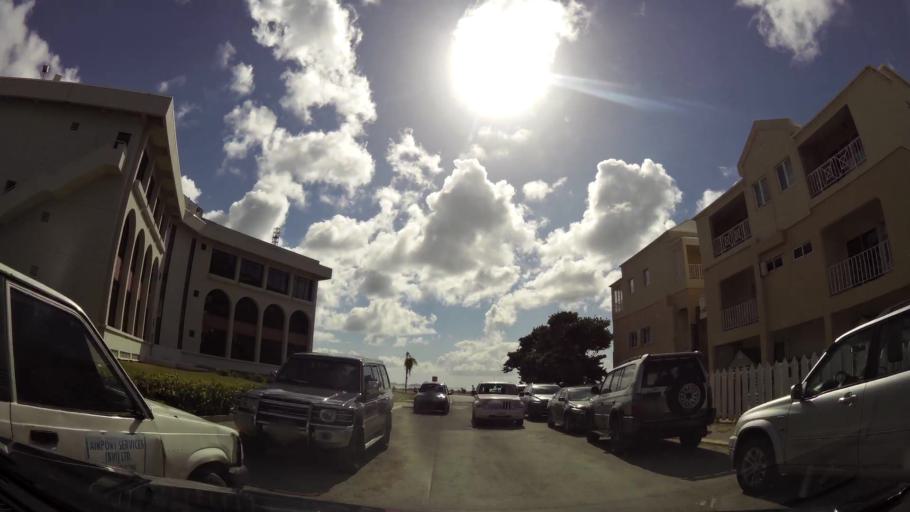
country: VG
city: Road Town
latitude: 18.4211
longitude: -64.6167
